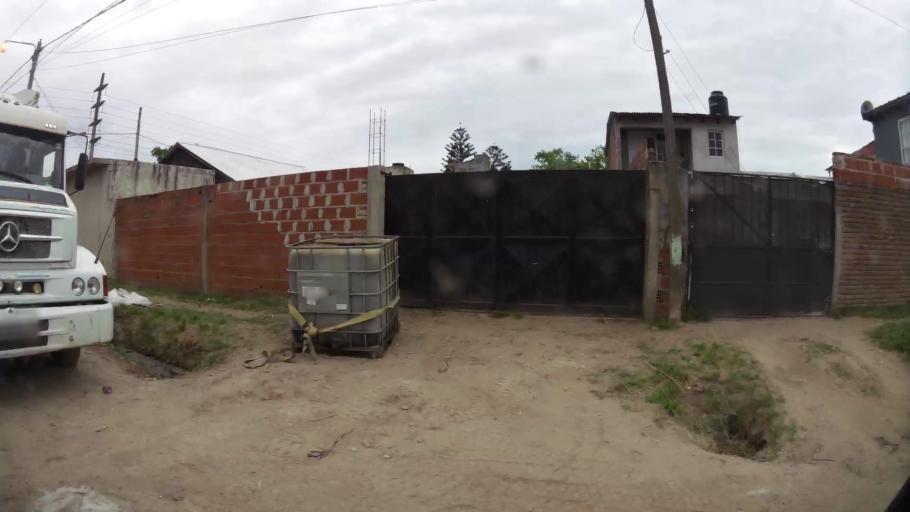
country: AR
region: Buenos Aires
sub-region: Partido de Zarate
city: Zarate
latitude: -34.1172
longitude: -59.0330
